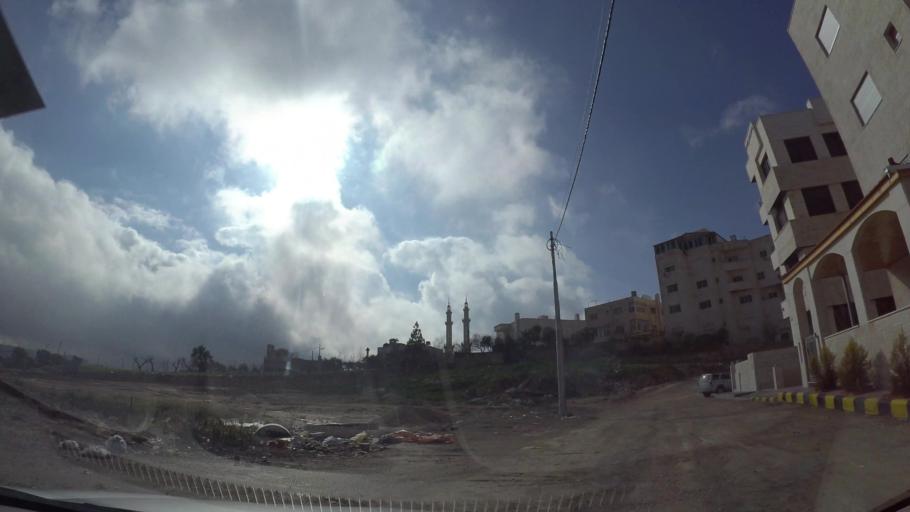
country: JO
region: Amman
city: Al Jubayhah
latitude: 32.0400
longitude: 35.8713
